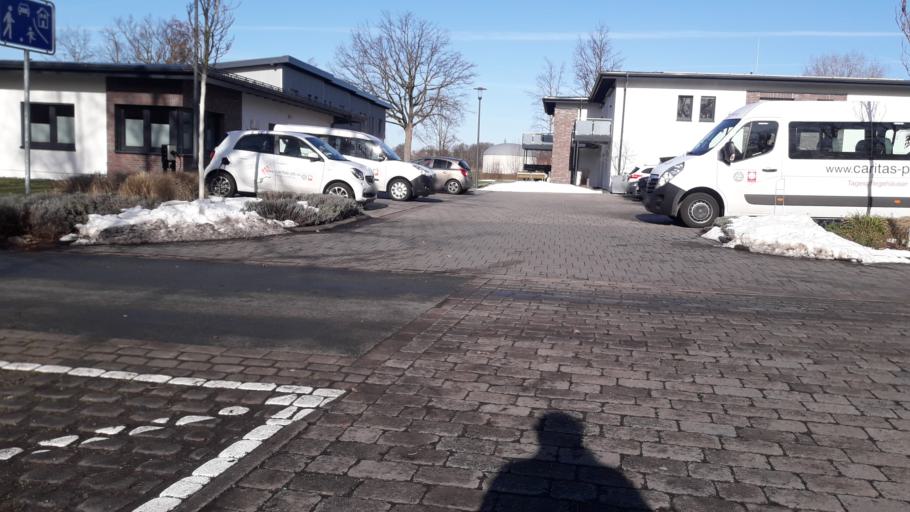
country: DE
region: North Rhine-Westphalia
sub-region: Regierungsbezirk Detmold
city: Delbruck
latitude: 51.7454
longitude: 8.5103
